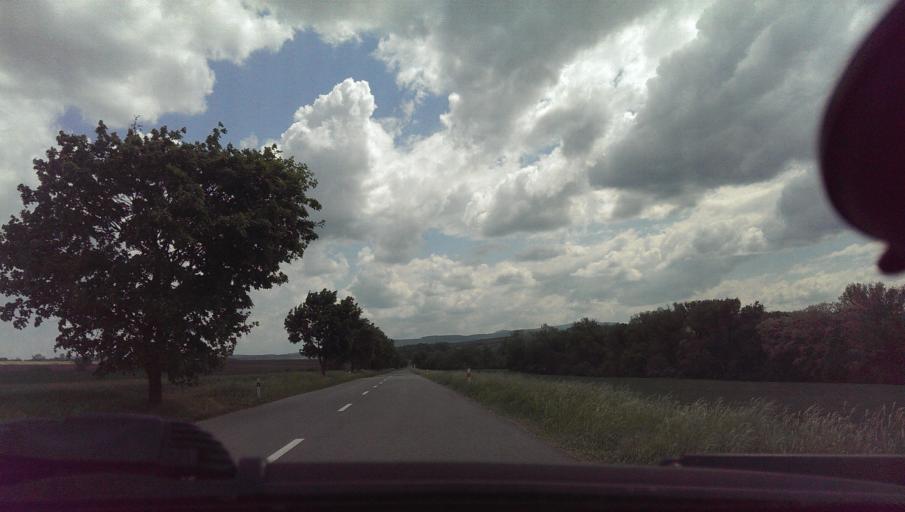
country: CZ
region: Zlin
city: Hluk
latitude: 48.9782
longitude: 17.5526
